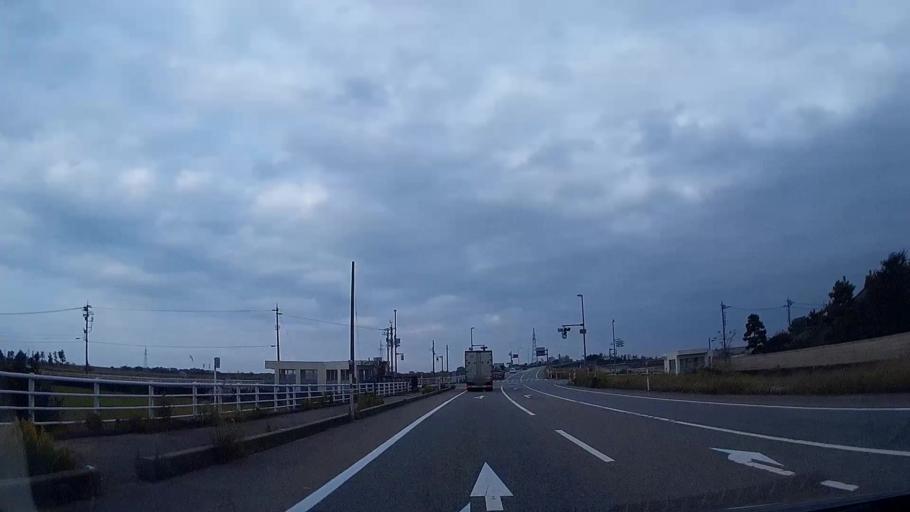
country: JP
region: Toyama
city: Nyuzen
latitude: 36.8986
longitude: 137.4452
